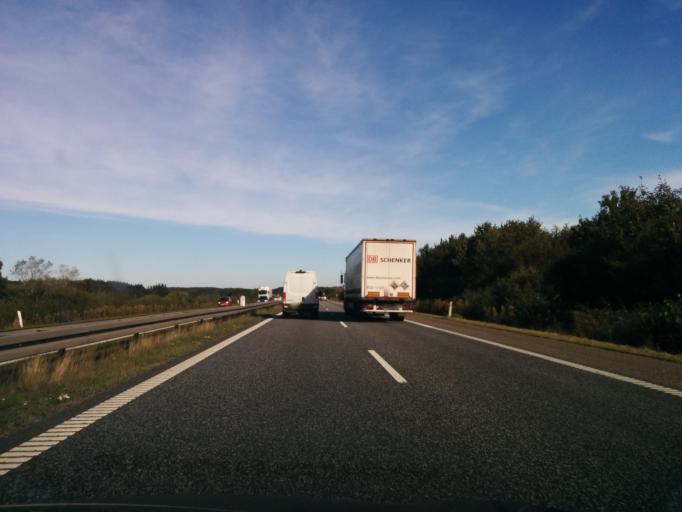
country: DK
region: South Denmark
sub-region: Fredericia Kommune
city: Taulov
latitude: 55.5730
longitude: 9.5654
